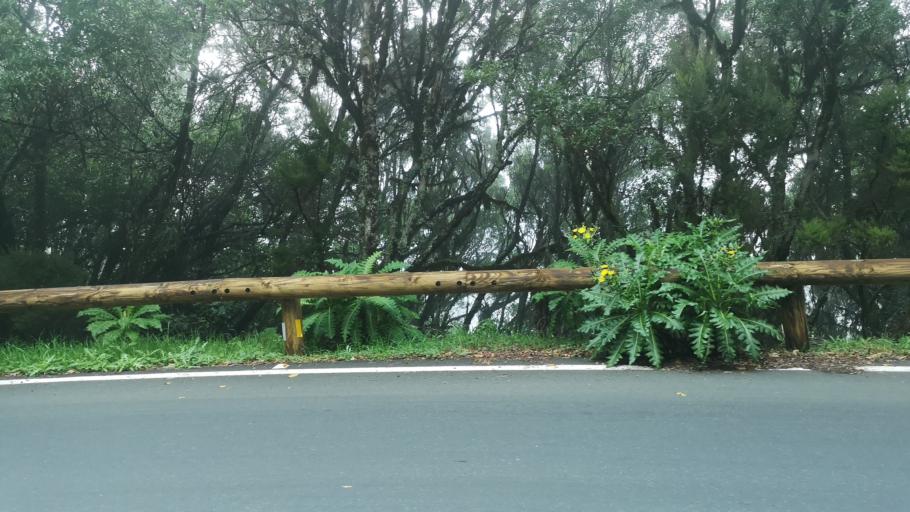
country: ES
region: Canary Islands
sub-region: Provincia de Santa Cruz de Tenerife
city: Alajero
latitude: 28.1099
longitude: -17.2248
